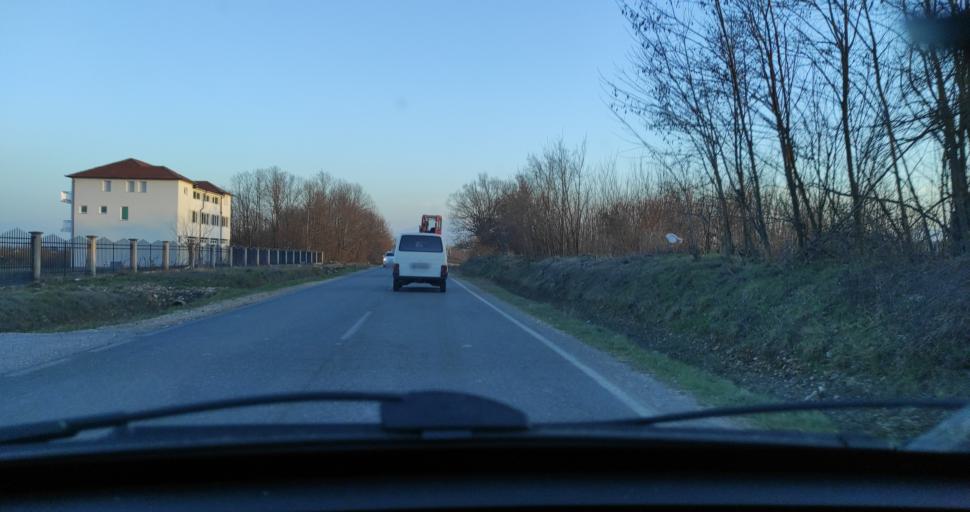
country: XK
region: Gjakova
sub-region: Komuna e Decanit
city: Gllogjan
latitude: 42.4417
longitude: 20.3670
